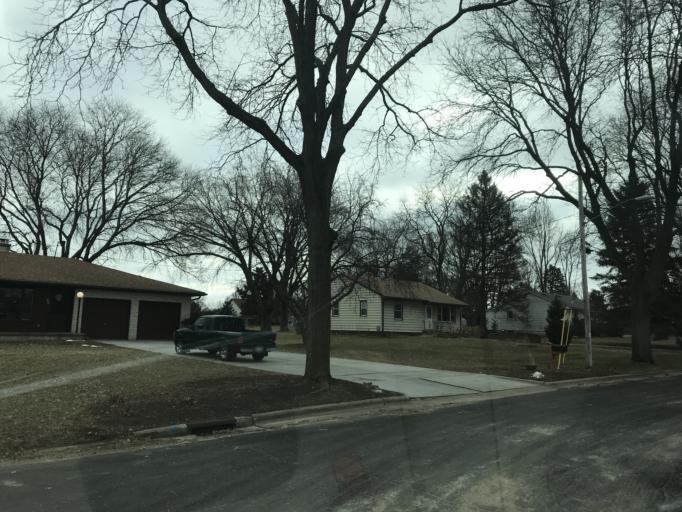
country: US
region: Wisconsin
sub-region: Dane County
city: Monona
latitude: 43.1101
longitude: -89.3023
